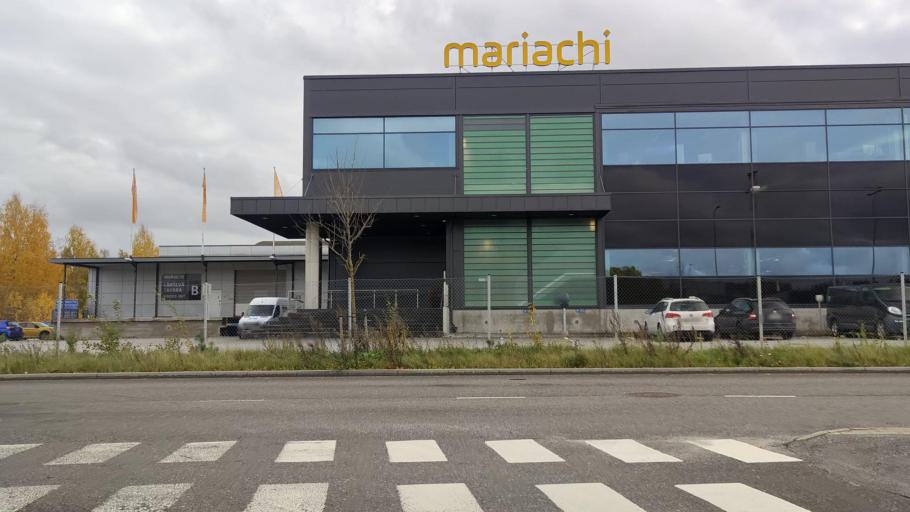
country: FI
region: Varsinais-Suomi
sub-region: Turku
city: Kaarina
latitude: 60.4651
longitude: 22.3479
